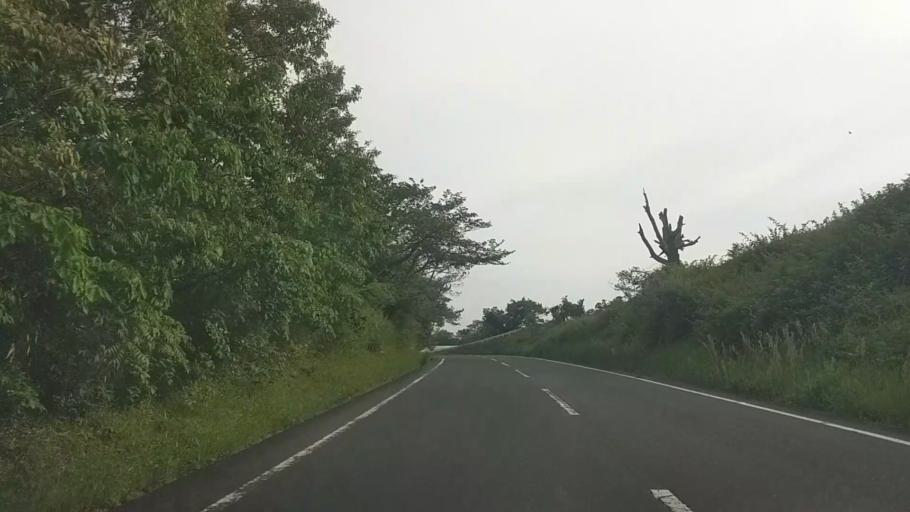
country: JP
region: Shizuoka
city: Kosai-shi
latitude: 34.7409
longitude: 137.5969
